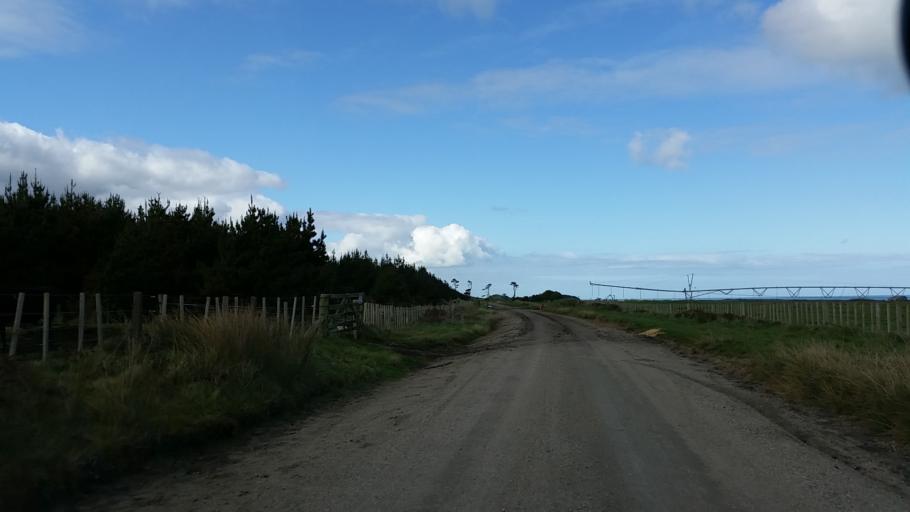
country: NZ
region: Taranaki
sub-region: South Taranaki District
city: Patea
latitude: -39.7968
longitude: 174.5906
